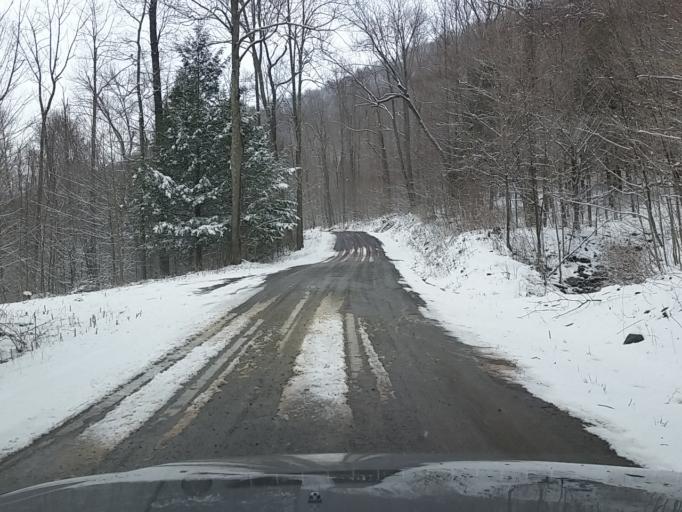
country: US
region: Pennsylvania
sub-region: Sullivan County
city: Laporte
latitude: 41.3339
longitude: -76.4609
